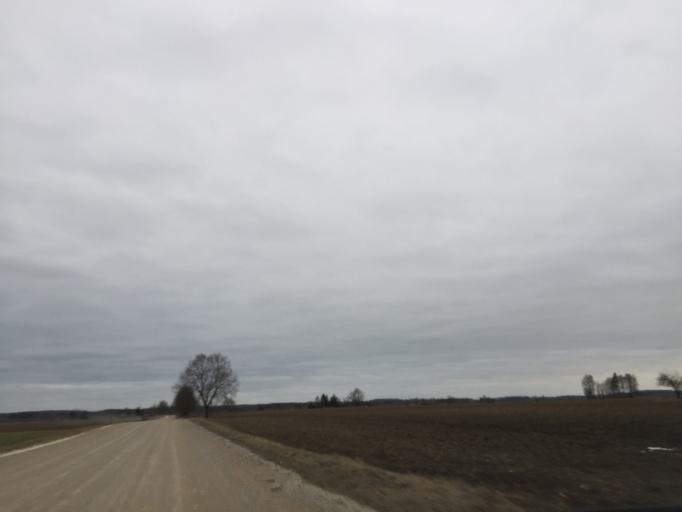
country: LT
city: Zagare
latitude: 56.2794
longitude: 23.2597
